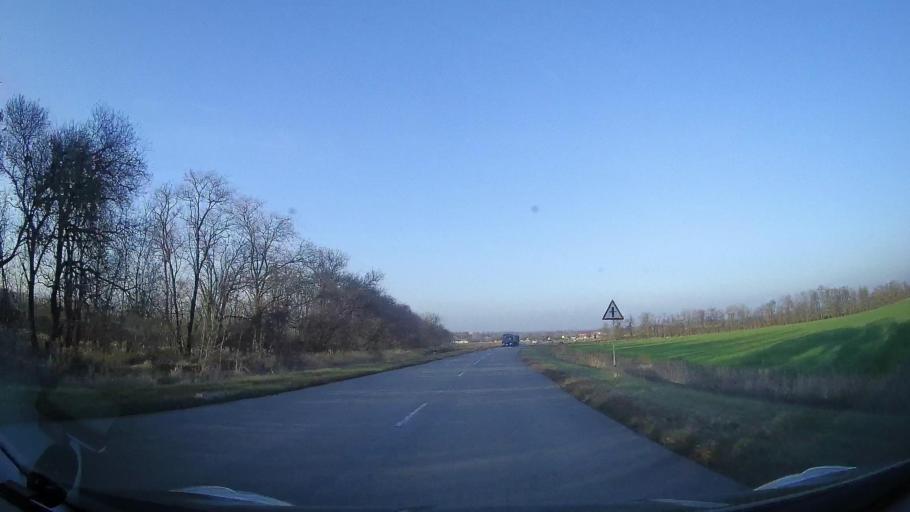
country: RU
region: Rostov
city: Kirovskaya
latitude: 47.0242
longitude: 39.9787
